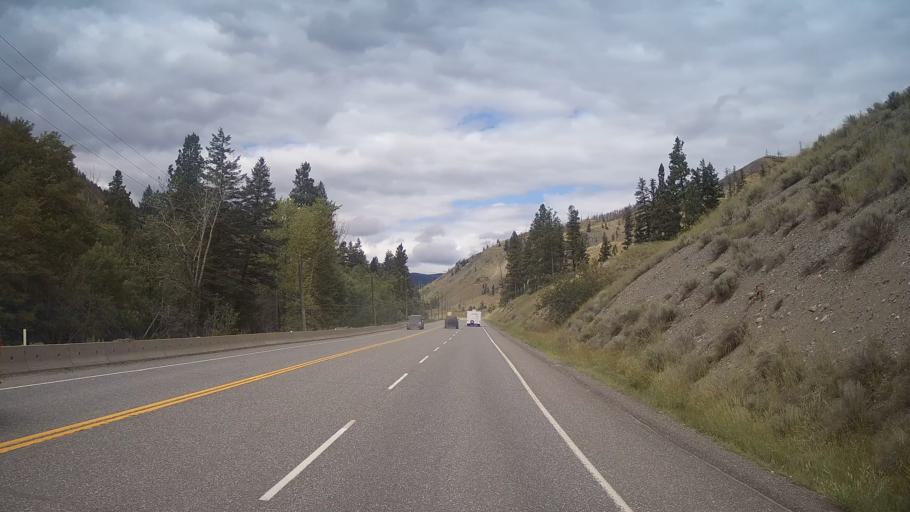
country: CA
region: British Columbia
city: Cache Creek
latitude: 50.9688
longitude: -121.4645
